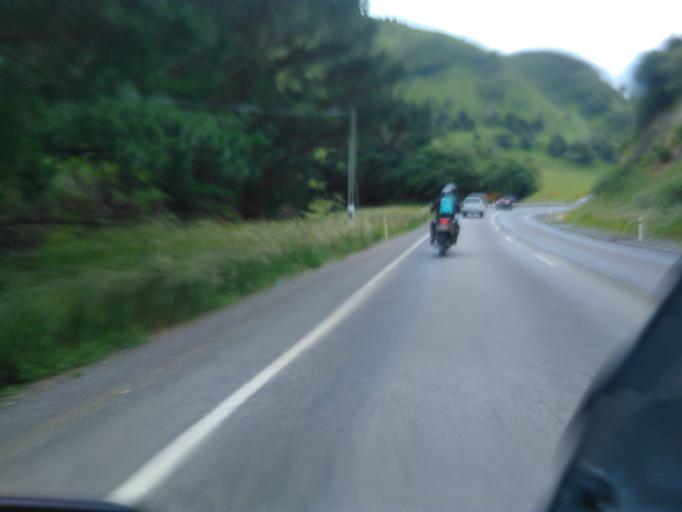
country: NZ
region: Bay of Plenty
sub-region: Opotiki District
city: Opotiki
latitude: -38.3783
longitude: 177.4792
